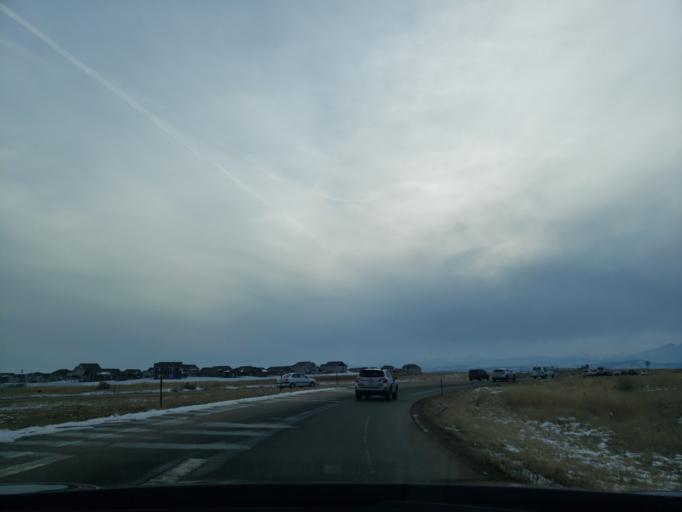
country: US
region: Colorado
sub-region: Larimer County
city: Campion
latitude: 40.3363
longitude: -105.0937
